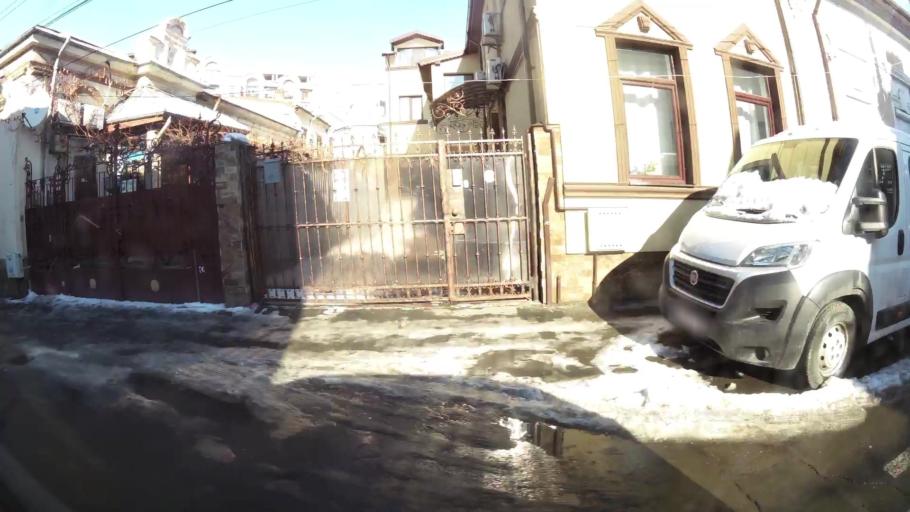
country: RO
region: Bucuresti
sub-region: Municipiul Bucuresti
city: Bucuresti
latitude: 44.4214
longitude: 26.0916
